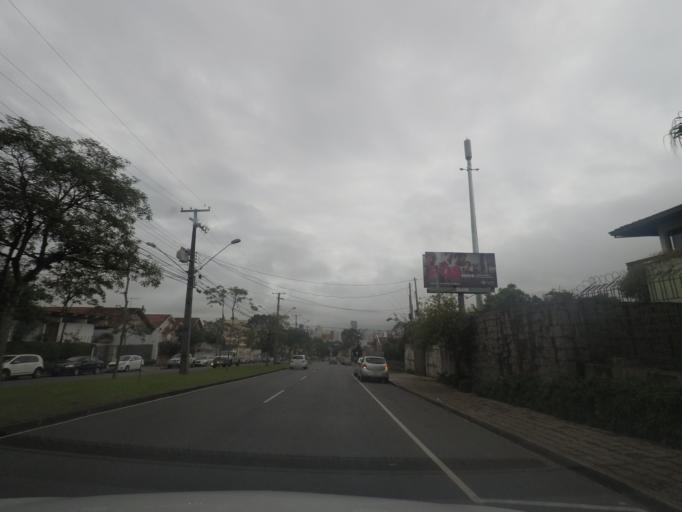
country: BR
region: Parana
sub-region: Curitiba
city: Curitiba
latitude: -25.4427
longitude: -49.2462
